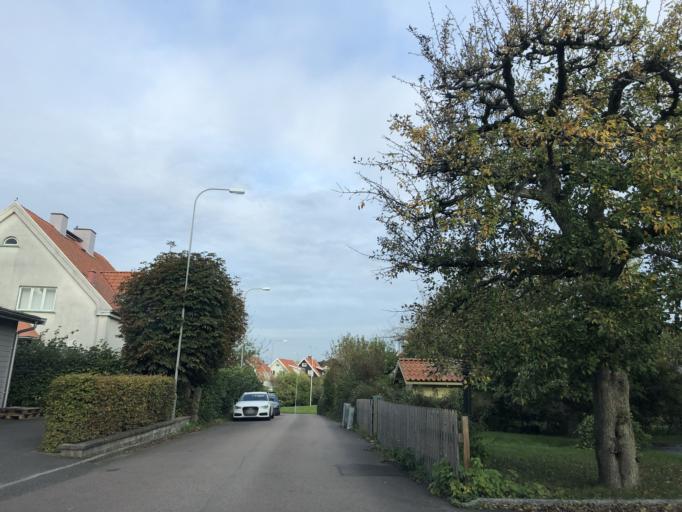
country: SE
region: Vaestra Goetaland
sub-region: Goteborg
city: Majorna
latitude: 57.6685
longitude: 11.8782
